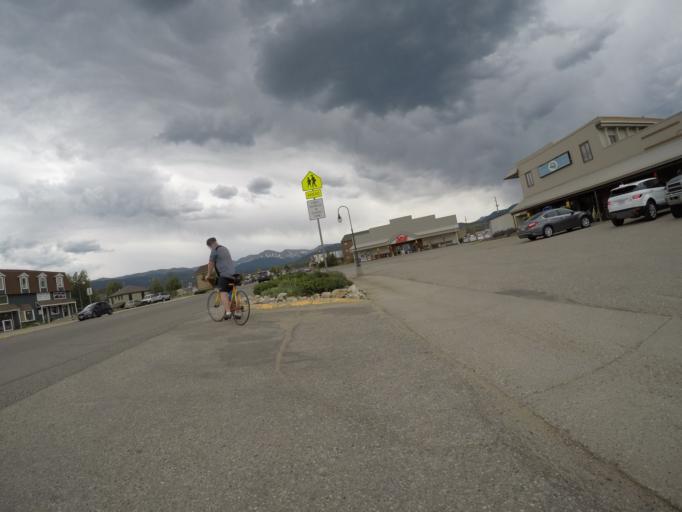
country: US
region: Colorado
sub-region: Grand County
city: Fraser
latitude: 39.9490
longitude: -105.8173
